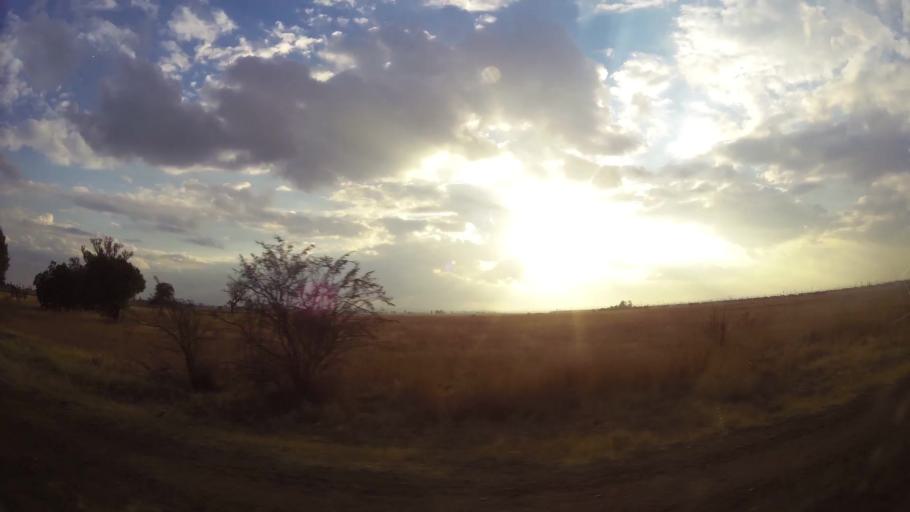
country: ZA
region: Gauteng
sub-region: Sedibeng District Municipality
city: Vanderbijlpark
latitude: -26.6229
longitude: 27.8114
